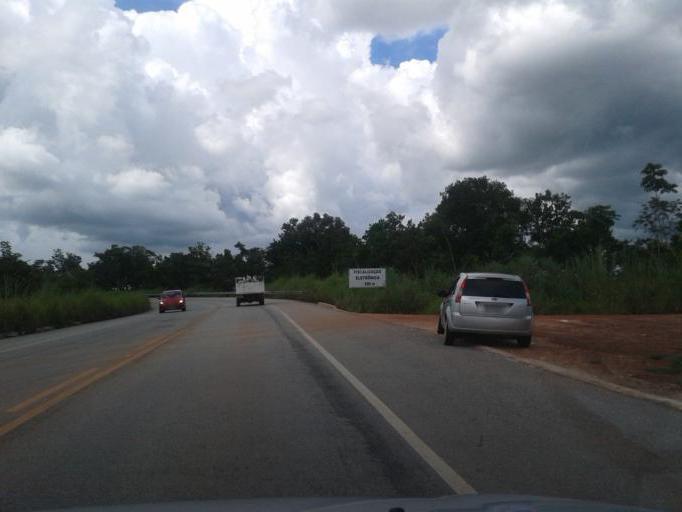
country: BR
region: Goias
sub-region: Goias
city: Goias
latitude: -15.8687
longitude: -50.0895
